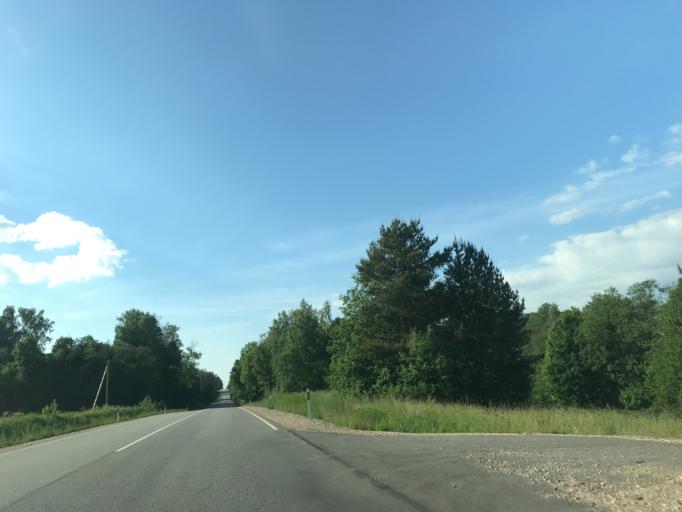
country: LV
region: Lielvarde
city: Lielvarde
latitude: 56.6541
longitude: 24.8778
